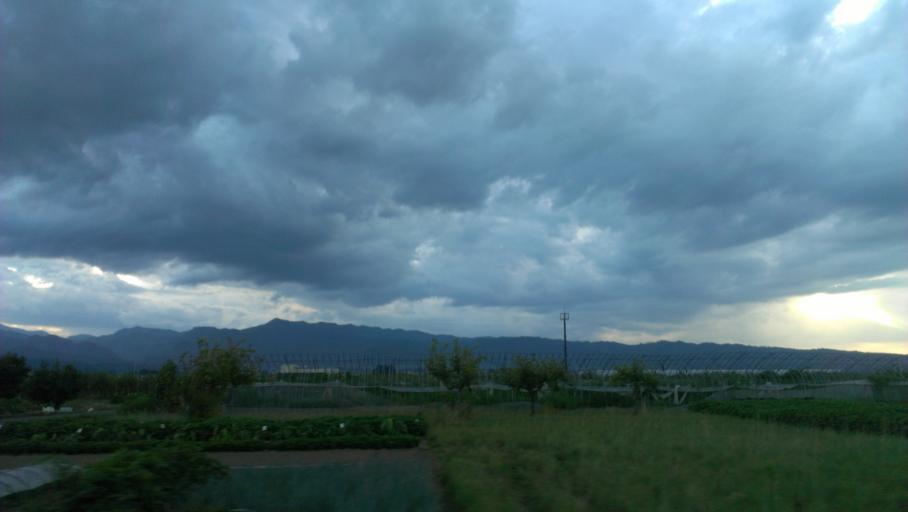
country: JP
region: Fukushima
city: Kitakata
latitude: 37.4533
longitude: 139.8808
